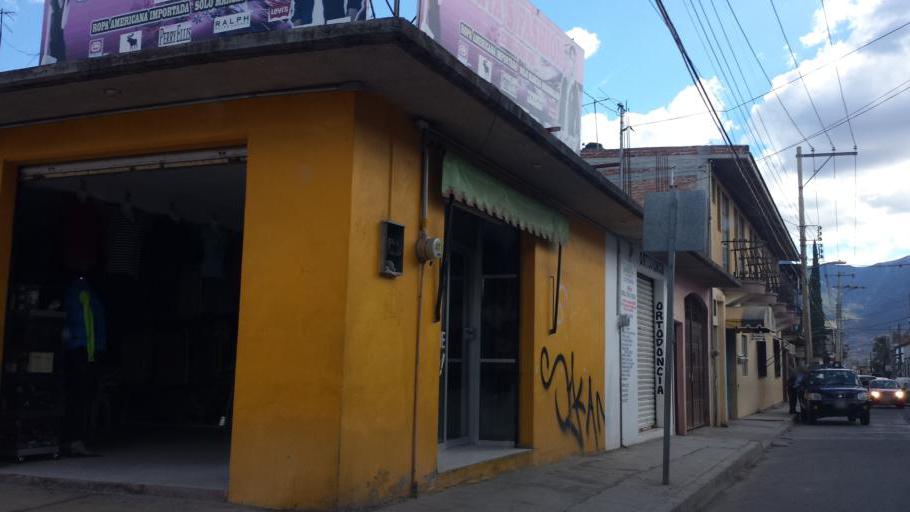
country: MX
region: Oaxaca
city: Tlacolula de Matamoros
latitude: 16.9582
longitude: -96.4795
